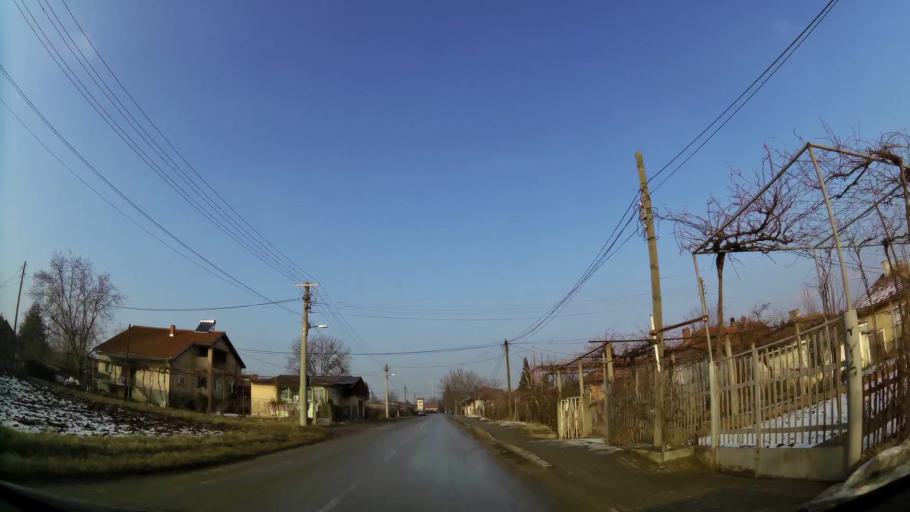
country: MK
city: Miladinovci
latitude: 41.9848
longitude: 21.6509
